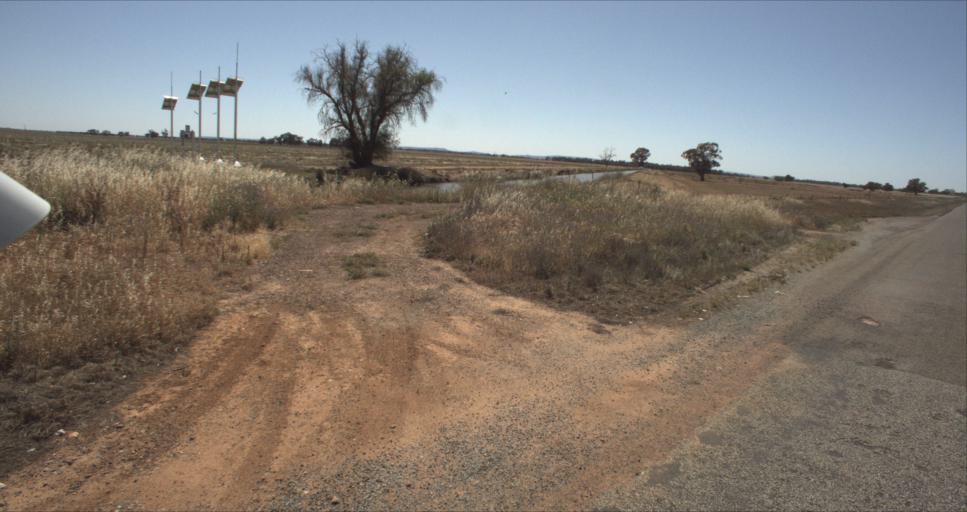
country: AU
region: New South Wales
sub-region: Leeton
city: Leeton
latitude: -34.5809
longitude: 146.2884
